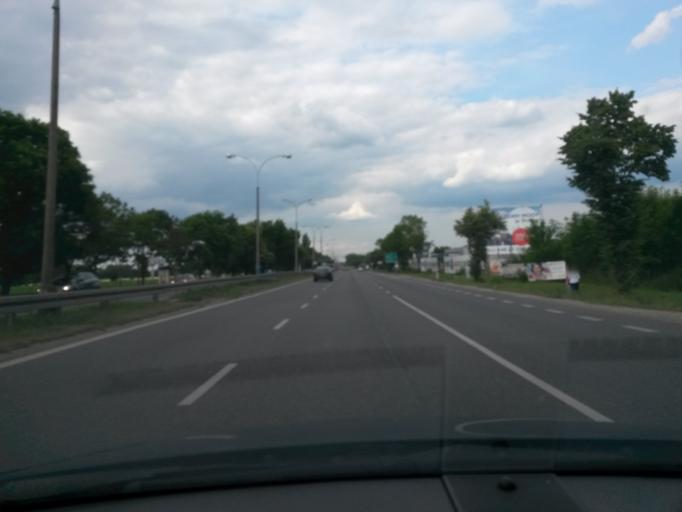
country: PL
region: Masovian Voivodeship
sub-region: Powiat pruszkowski
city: Nowe Grocholice
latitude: 52.1391
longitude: 20.9018
